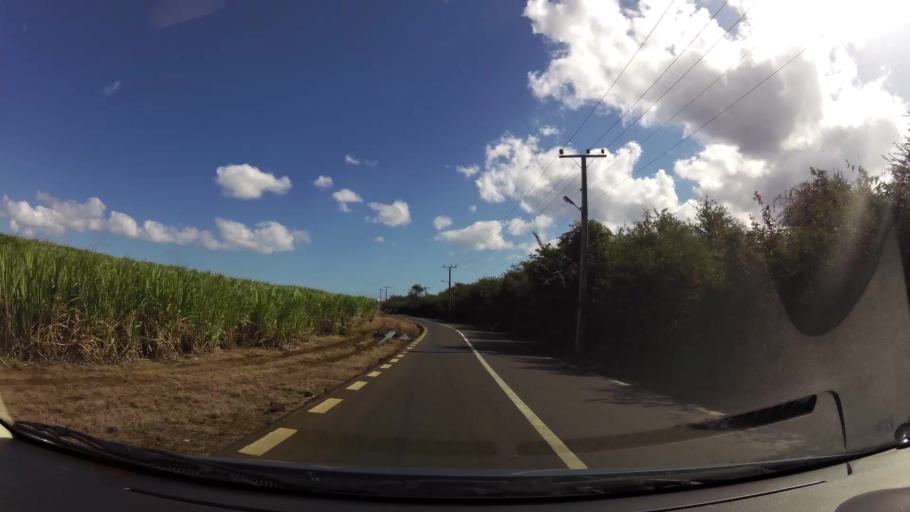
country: MU
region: Black River
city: Gros Cailloux
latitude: -20.2216
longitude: 57.4228
